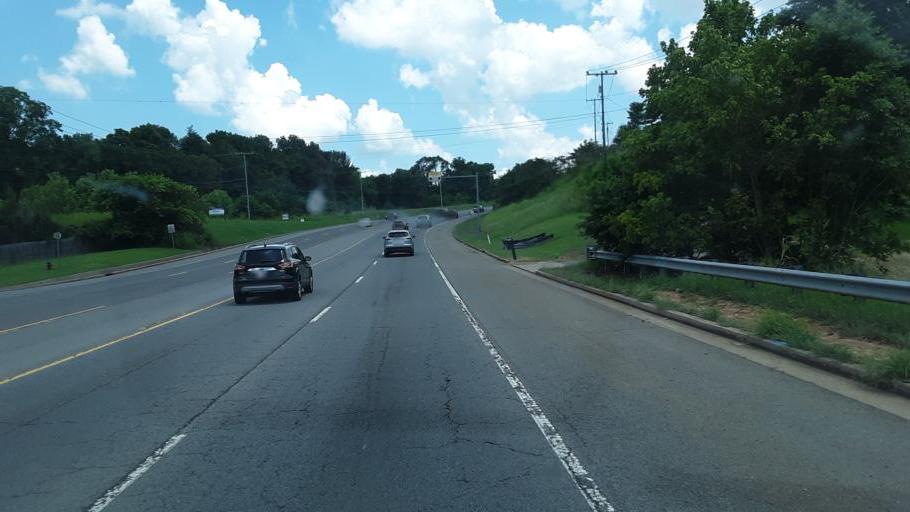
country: US
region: Kentucky
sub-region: Christian County
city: Oak Grove
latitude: 36.6256
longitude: -87.3653
